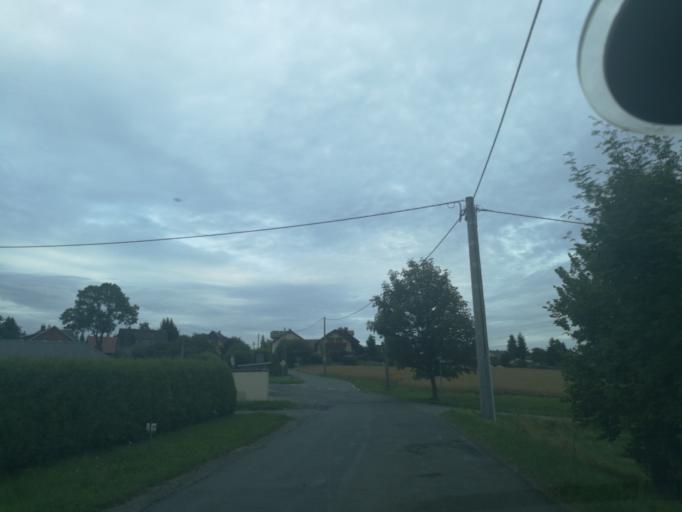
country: DE
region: Saxony
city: Adorf
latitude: 50.3085
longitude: 12.2721
